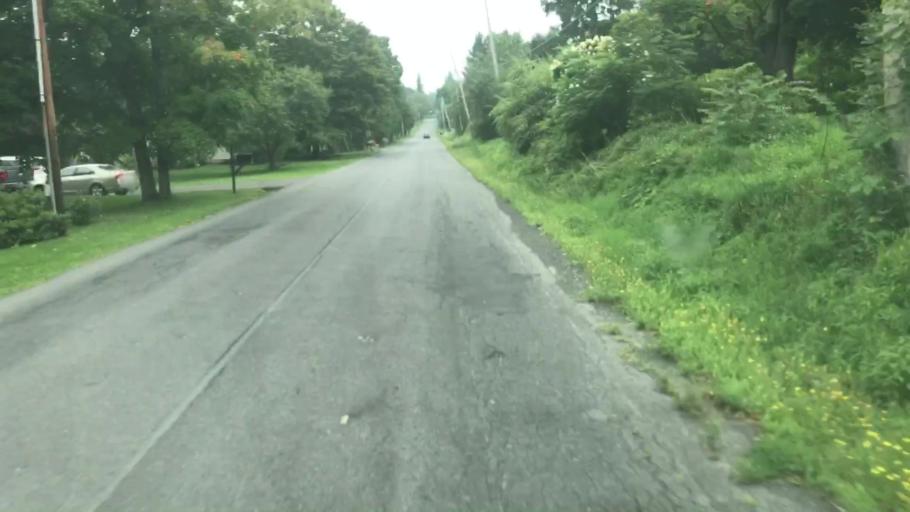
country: US
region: New York
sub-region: Onondaga County
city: Skaneateles
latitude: 42.9481
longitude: -76.4450
